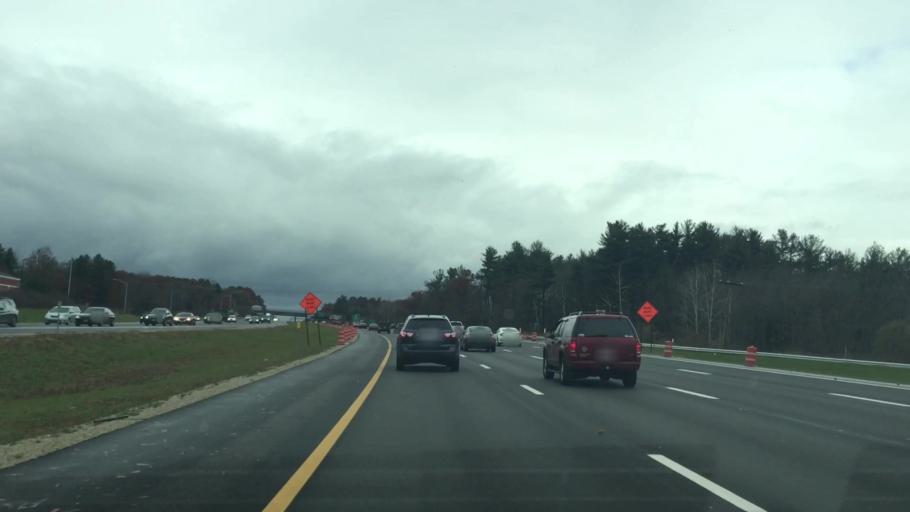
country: US
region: New Hampshire
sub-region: Rockingham County
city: Hampton Falls
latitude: 42.9354
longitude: -70.8619
